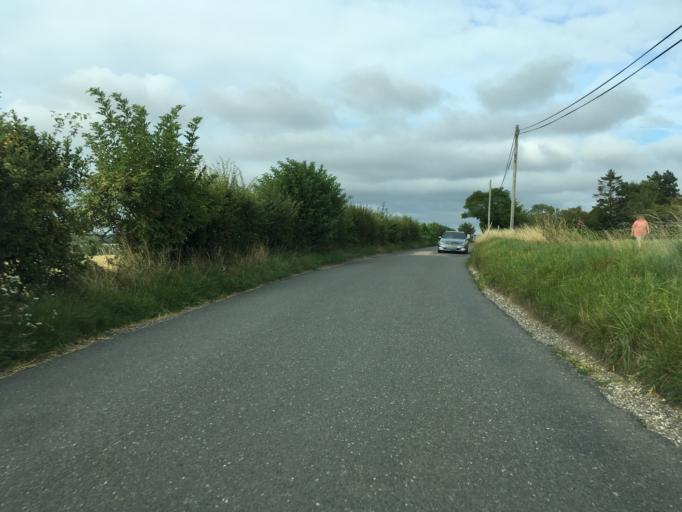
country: GB
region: England
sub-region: Hampshire
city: Colden Common
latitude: 51.0125
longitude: -1.2590
